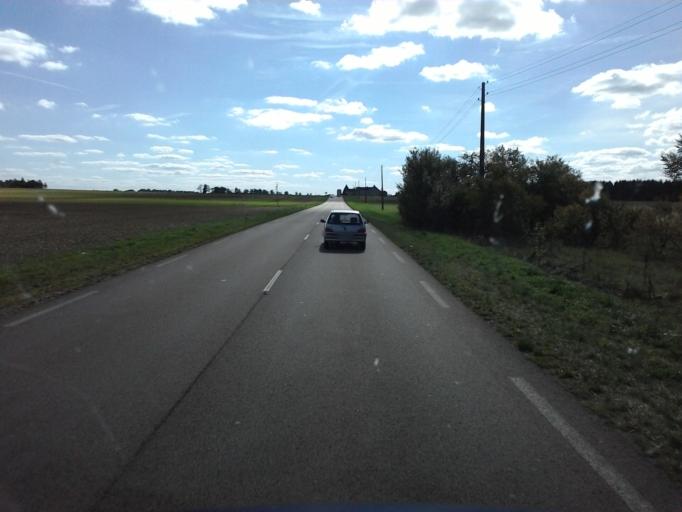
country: FR
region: Bourgogne
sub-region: Departement de la Cote-d'Or
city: Chatillon-sur-Seine
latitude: 47.8359
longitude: 4.5473
